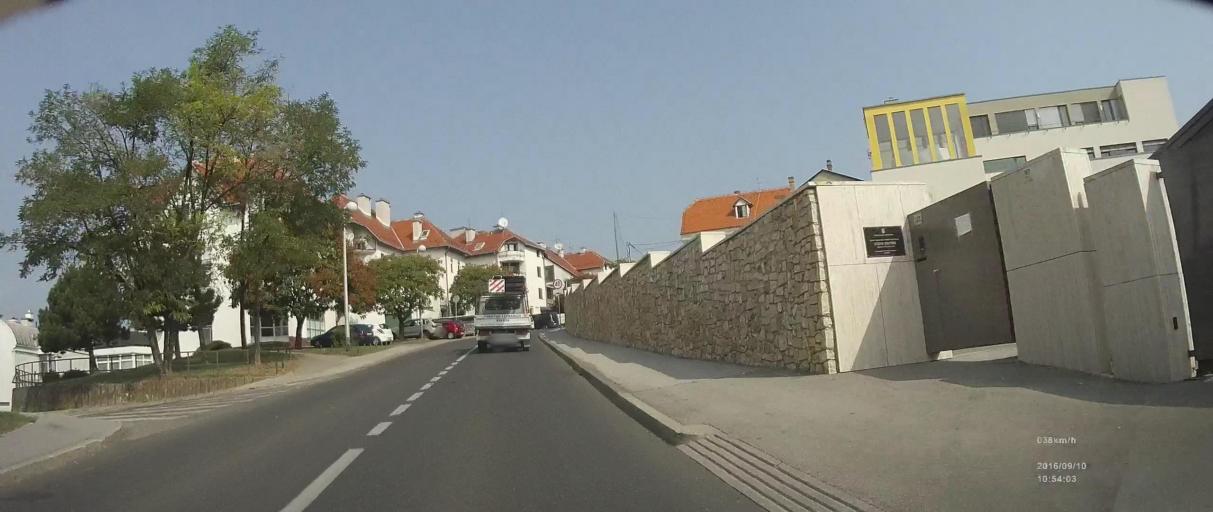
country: HR
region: Grad Zagreb
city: Zagreb - Centar
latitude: 45.8257
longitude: 15.9378
